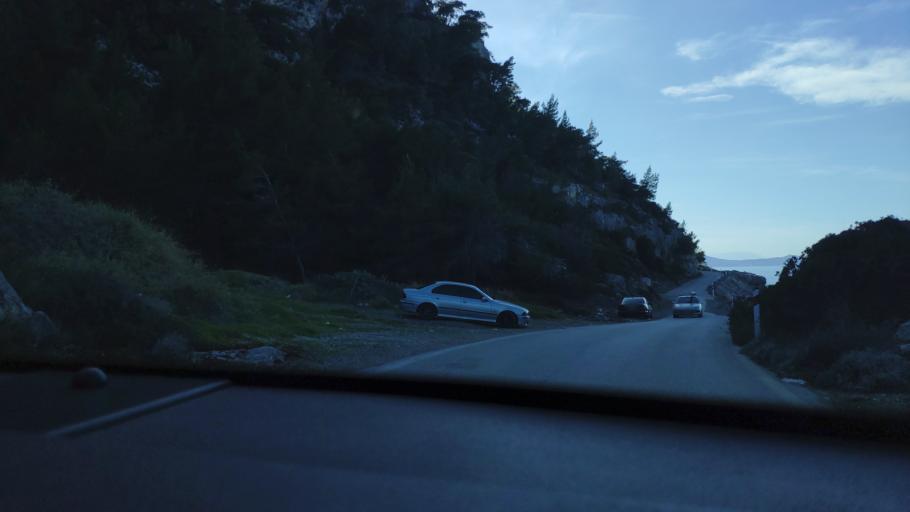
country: GR
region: Attica
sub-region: Nomarchia Dytikis Attikis
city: Kineta
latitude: 38.0638
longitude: 23.1281
